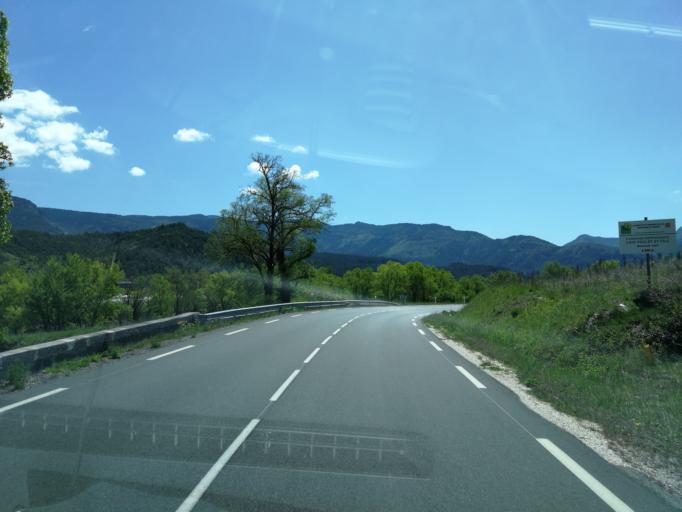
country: FR
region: Rhone-Alpes
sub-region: Departement de la Drome
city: Die
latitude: 44.7251
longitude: 5.2671
